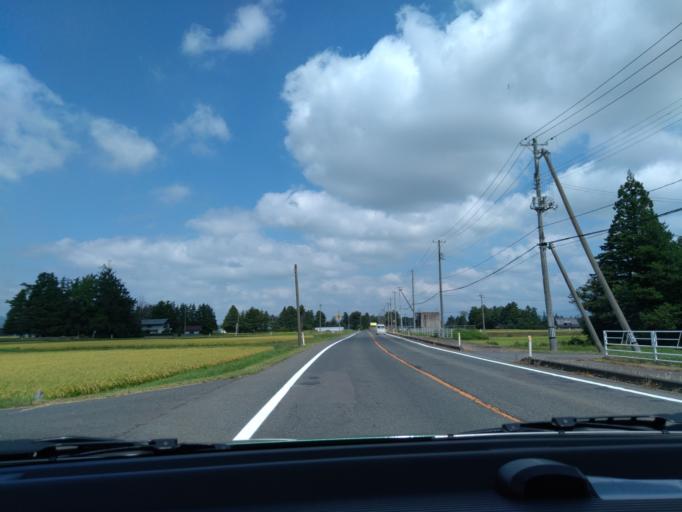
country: JP
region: Iwate
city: Hanamaki
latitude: 39.4281
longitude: 141.0900
